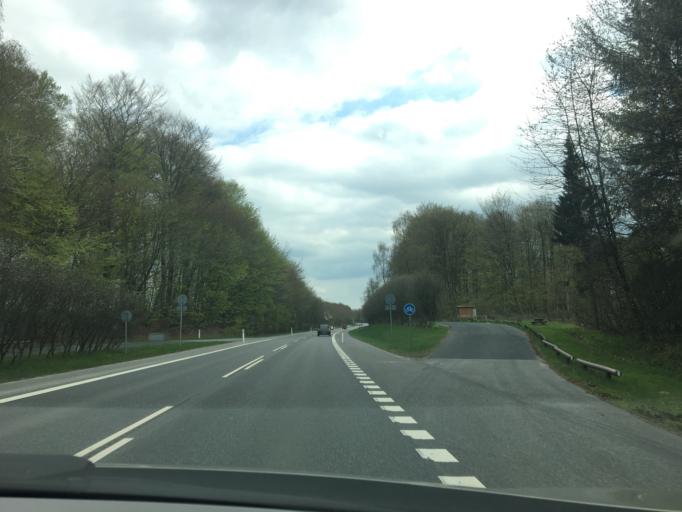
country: DK
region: Central Jutland
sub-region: Horsens Kommune
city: Braedstrup
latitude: 55.9575
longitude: 9.6204
